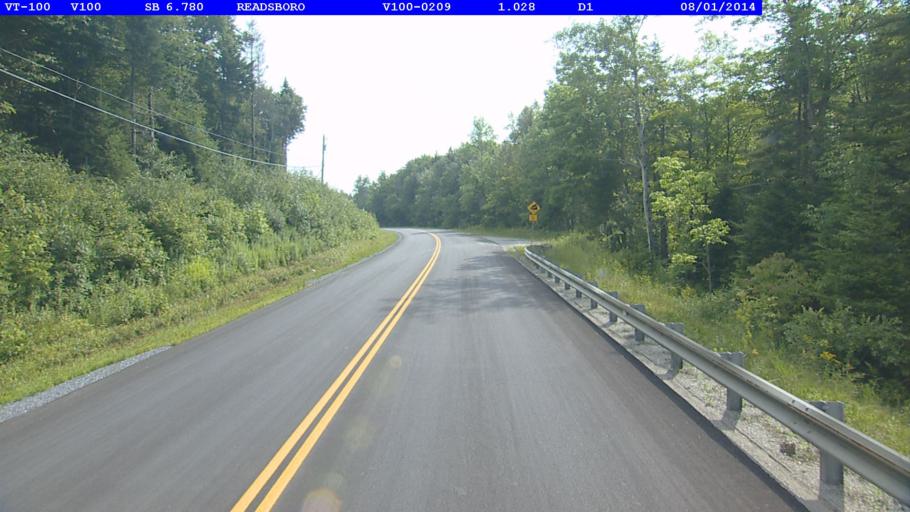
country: US
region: Massachusetts
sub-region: Berkshire County
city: North Adams
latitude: 42.8207
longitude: -73.0052
